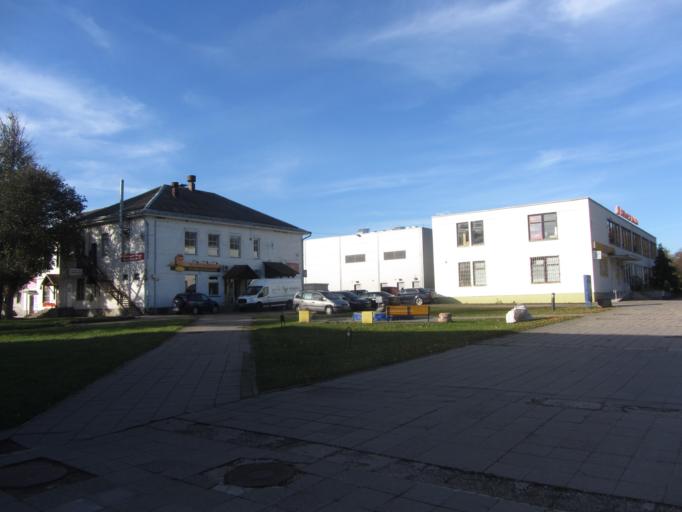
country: LT
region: Vilnius County
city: Elektrenai
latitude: 54.7841
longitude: 24.6587
